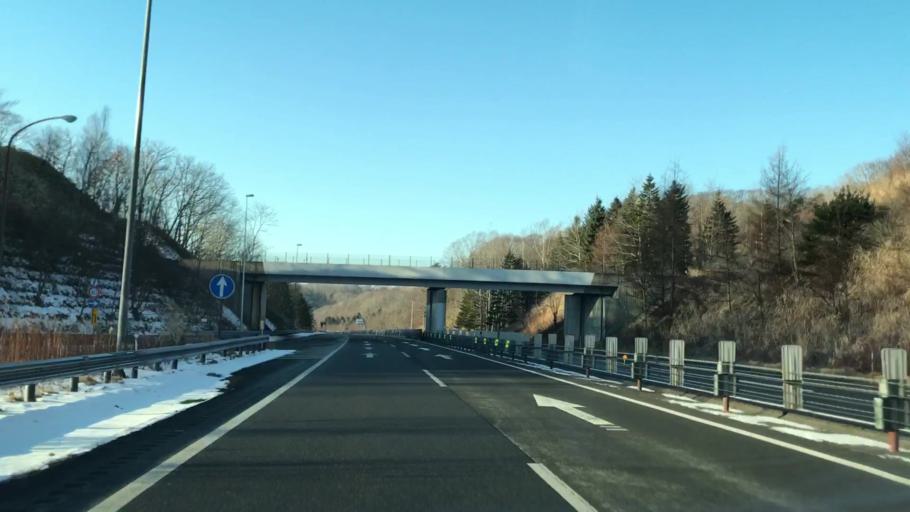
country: JP
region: Hokkaido
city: Shiraoi
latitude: 42.4620
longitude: 141.1745
